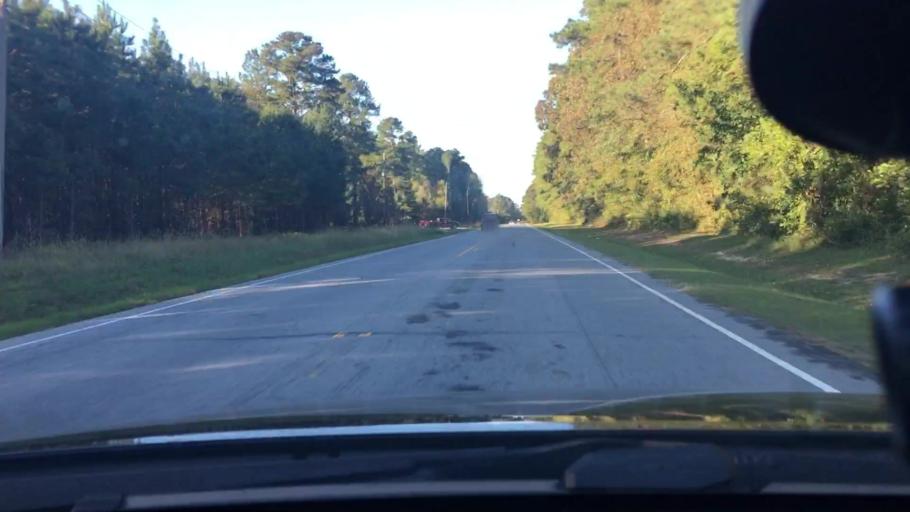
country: US
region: North Carolina
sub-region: Pitt County
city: Windsor
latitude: 35.4393
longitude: -77.2632
